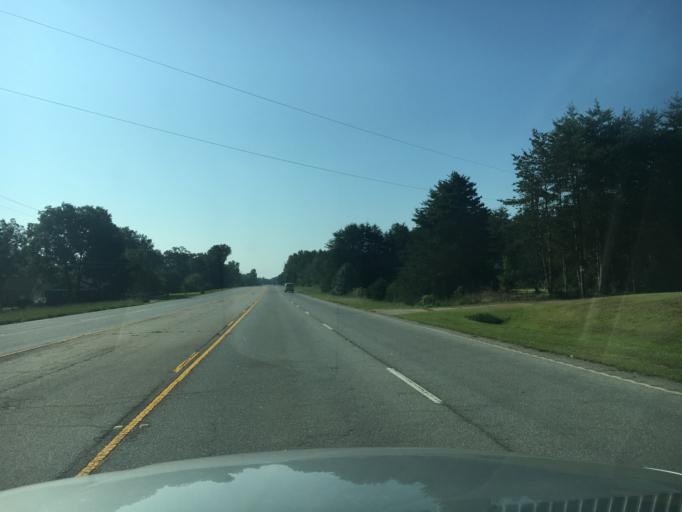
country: US
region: South Carolina
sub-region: Anderson County
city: Williamston
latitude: 34.5851
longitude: -82.3419
